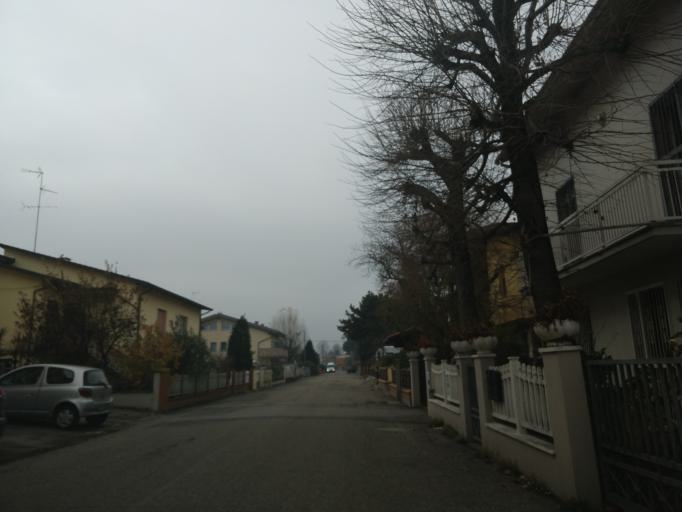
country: IT
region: Emilia-Romagna
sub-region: Provincia di Ferrara
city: Cento
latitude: 44.7188
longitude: 11.2884
